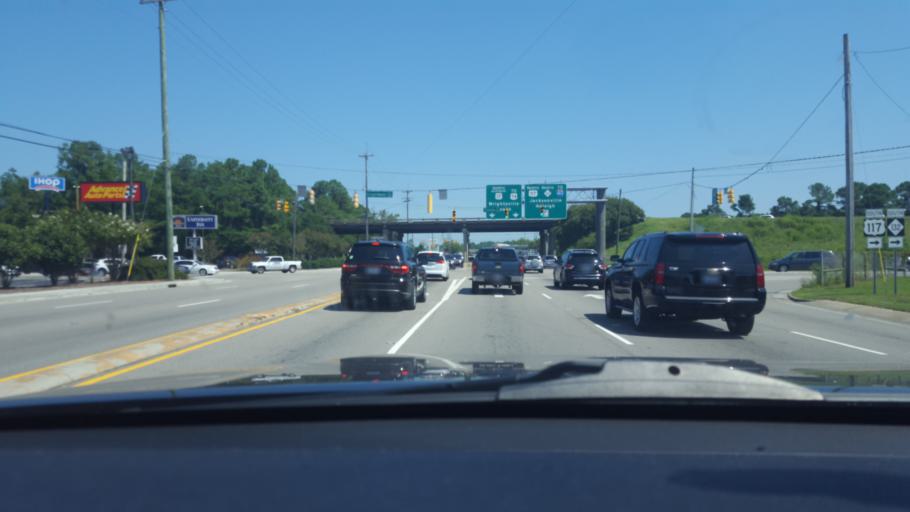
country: US
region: North Carolina
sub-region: New Hanover County
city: Kings Grant
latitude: 34.2458
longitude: -77.8725
